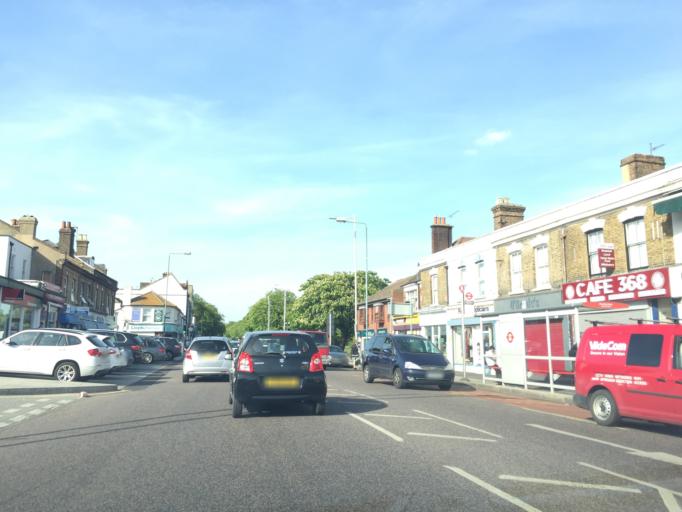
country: GB
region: England
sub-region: Greater London
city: Woodford Green
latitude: 51.6090
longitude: 0.0211
